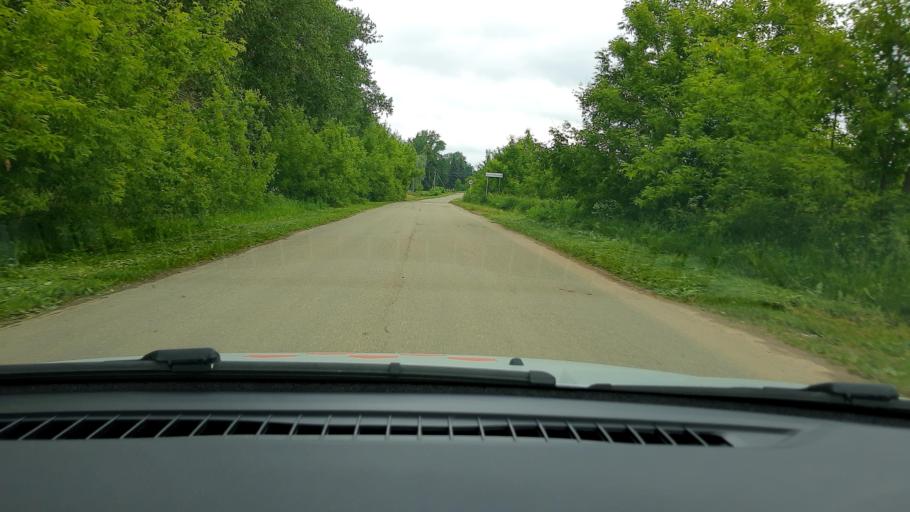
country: RU
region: Nizjnij Novgorod
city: Bogorodsk
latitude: 56.0696
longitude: 43.5043
